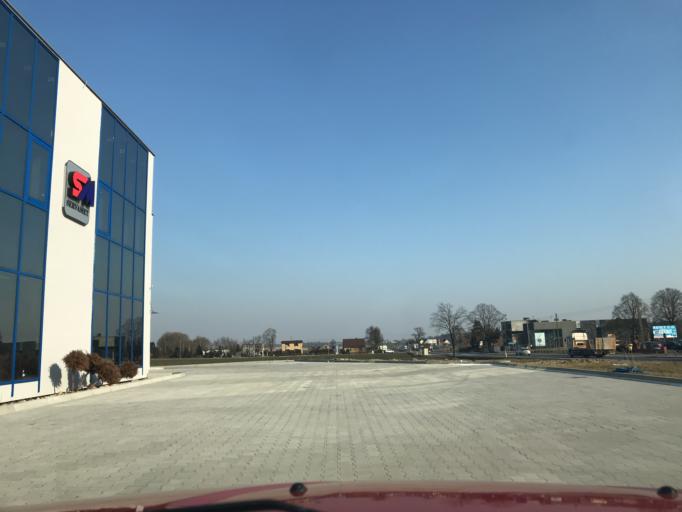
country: PL
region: Greater Poland Voivodeship
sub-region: Powiat pleszewski
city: Pleszew
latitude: 51.8938
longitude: 17.8196
